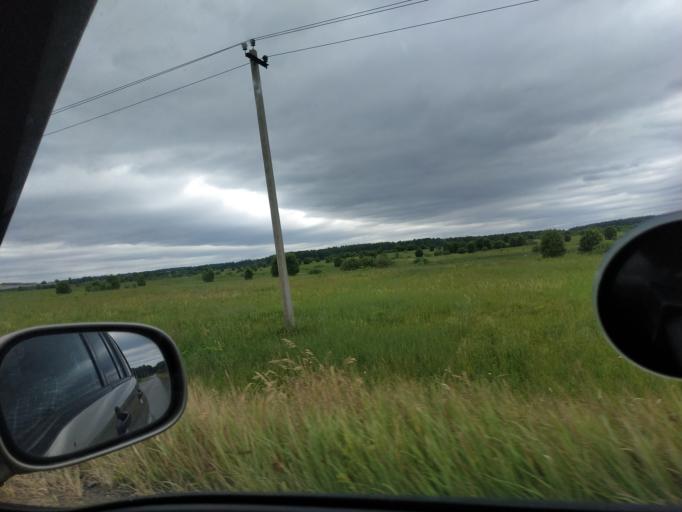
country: RU
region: Moskovskaya
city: Krasnoarmeysk
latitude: 56.0821
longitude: 38.2383
